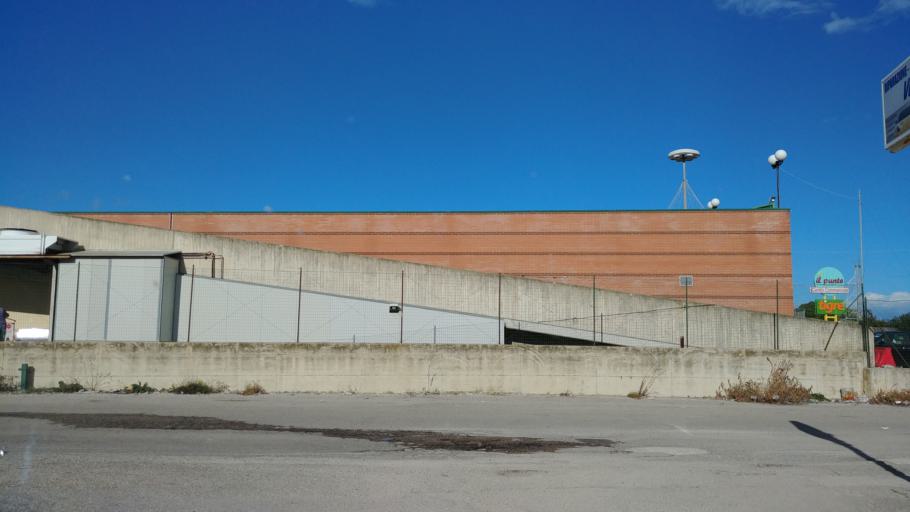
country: IT
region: Molise
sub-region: Provincia di Campobasso
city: Termoli
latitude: 41.9791
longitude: 15.0071
